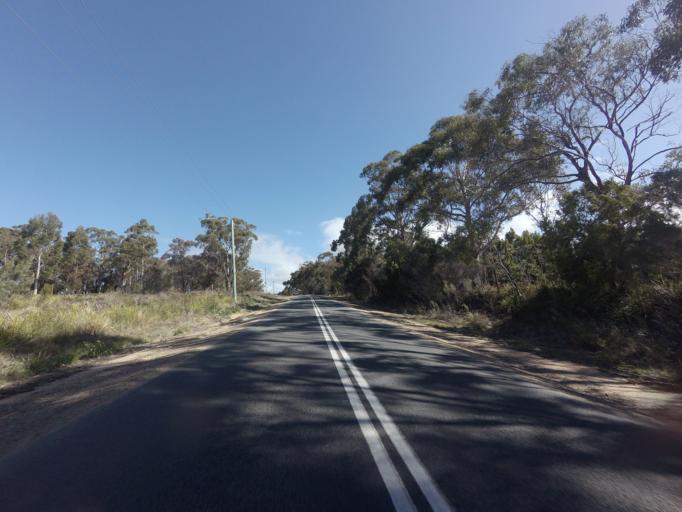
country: AU
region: Tasmania
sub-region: Break O'Day
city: St Helens
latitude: -41.6873
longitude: 148.2809
